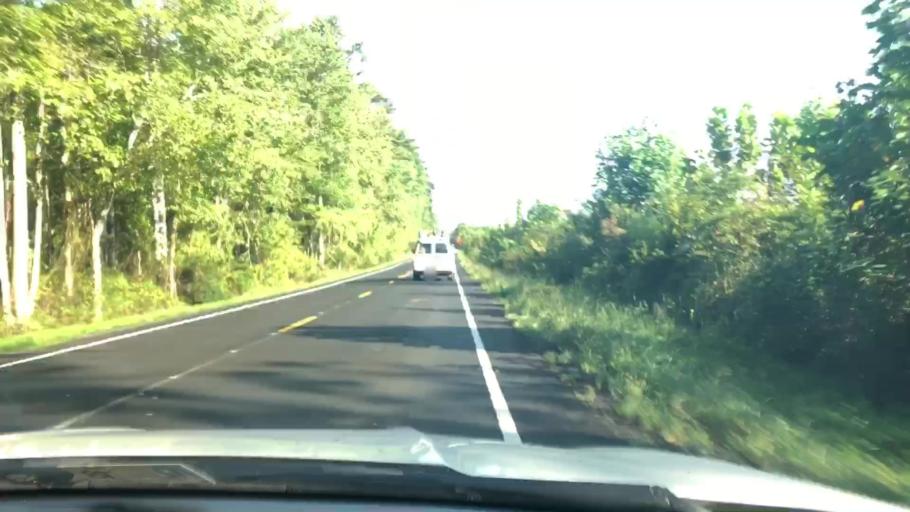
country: US
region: Virginia
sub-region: King William County
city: West Point
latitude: 37.4716
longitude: -76.8449
